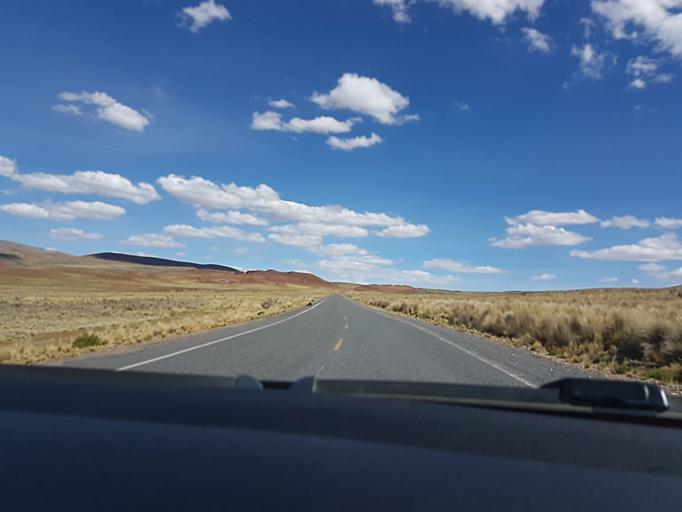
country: BO
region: La Paz
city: Tiahuanaco
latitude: -16.9974
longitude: -68.4254
